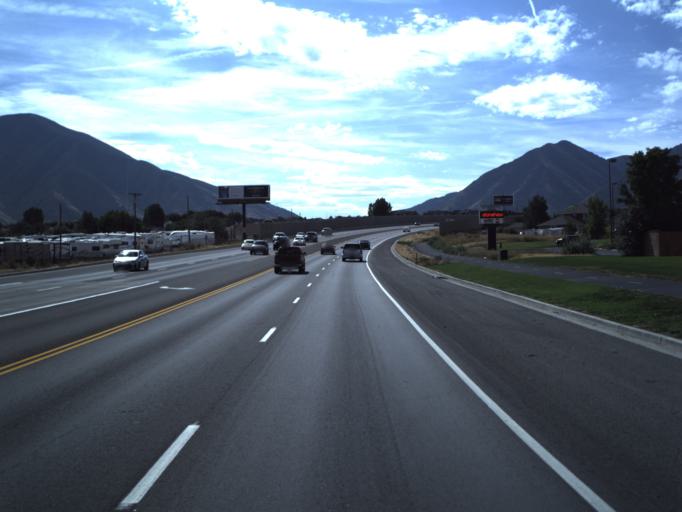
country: US
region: Utah
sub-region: Utah County
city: Spanish Fork
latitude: 40.1201
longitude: -111.6398
